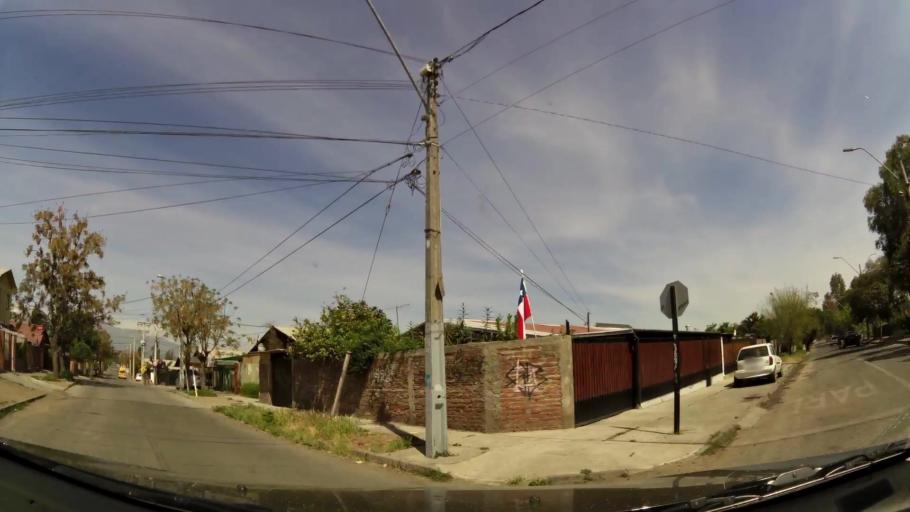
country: CL
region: Santiago Metropolitan
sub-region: Provincia de Cordillera
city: Puente Alto
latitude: -33.6128
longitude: -70.5574
